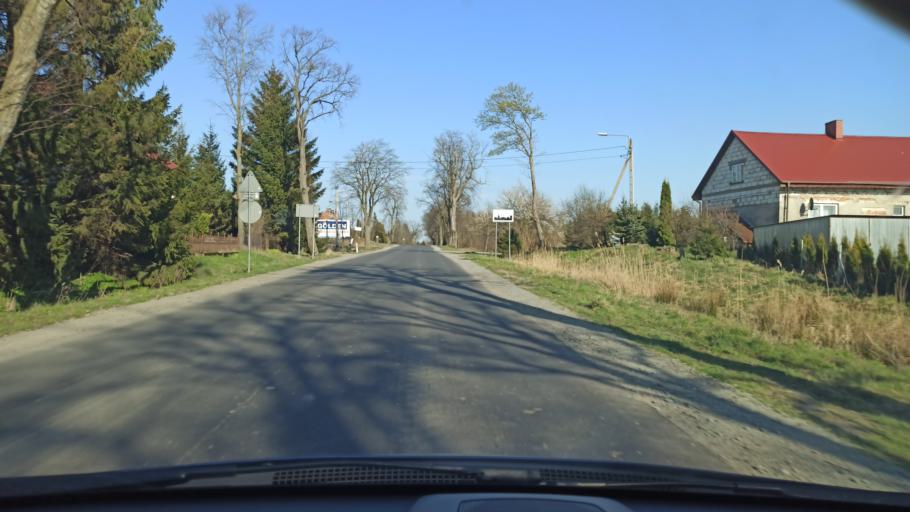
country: PL
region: Warmian-Masurian Voivodeship
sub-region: Powiat elblaski
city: Tolkmicko
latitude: 54.2161
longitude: 19.5305
